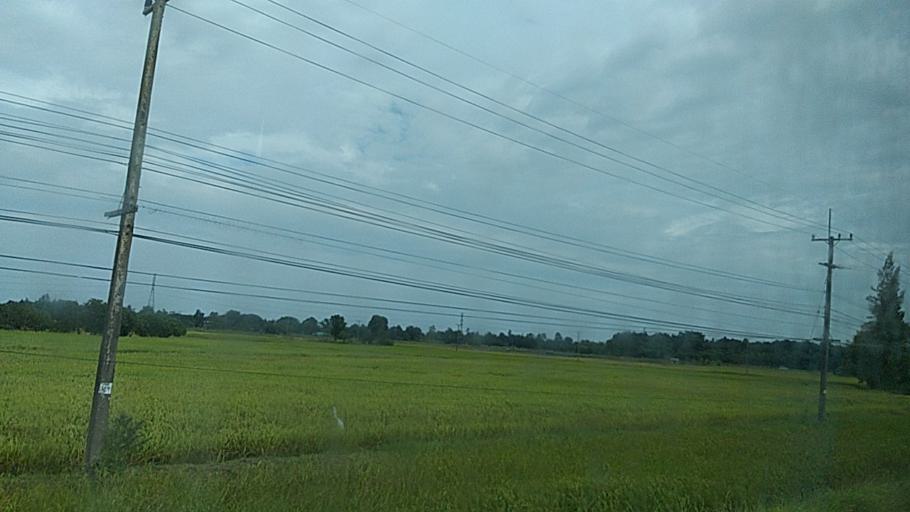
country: TH
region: Kalasin
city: Khong Chai
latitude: 16.1356
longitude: 103.4474
